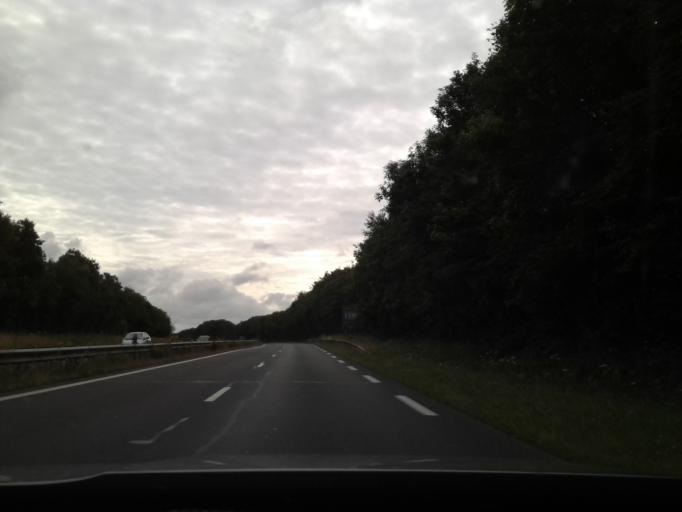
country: FR
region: Lower Normandy
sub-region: Departement du Calvados
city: Isigny-sur-Mer
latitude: 49.3079
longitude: -1.1081
